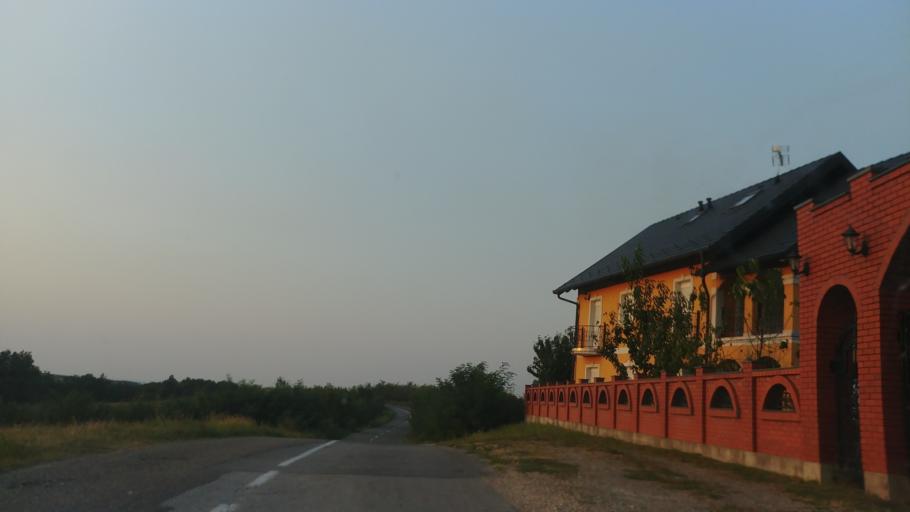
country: BA
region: Republika Srpska
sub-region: Opstina Ugljevik
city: Ugljevik
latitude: 44.7142
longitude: 18.9896
